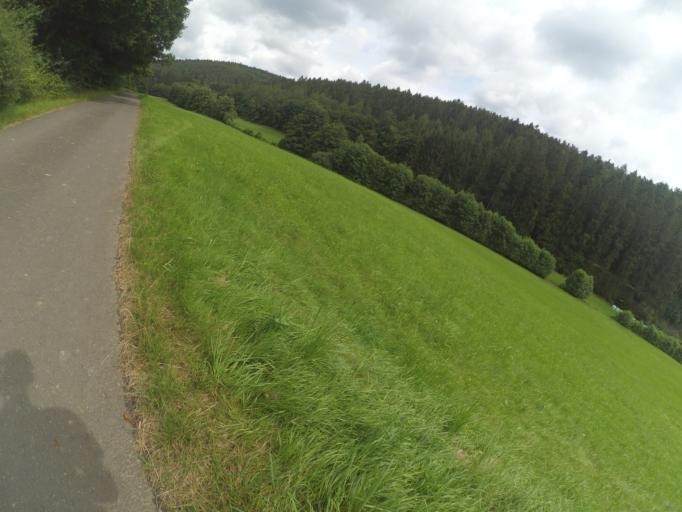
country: DE
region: Hesse
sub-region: Regierungsbezirk Kassel
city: Kirchheim
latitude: 50.8608
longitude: 9.5402
